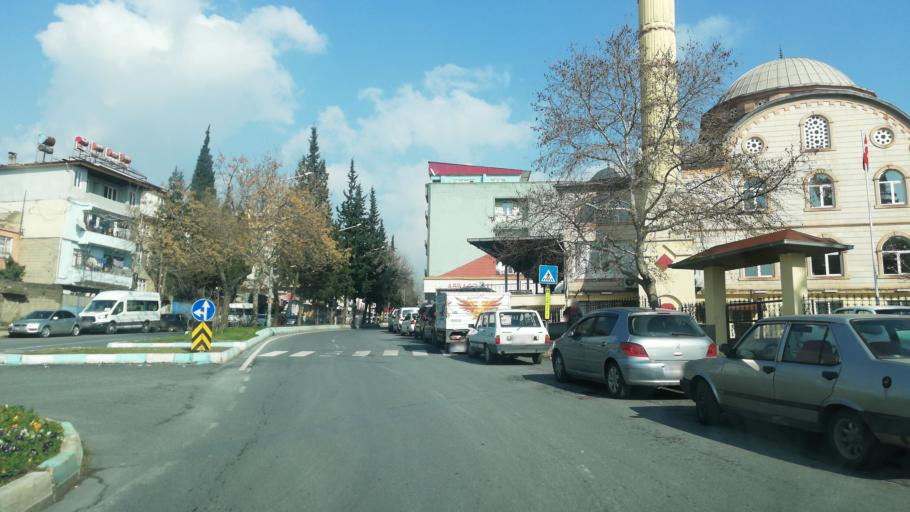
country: TR
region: Kahramanmaras
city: Kahramanmaras
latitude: 37.5786
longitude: 36.9350
